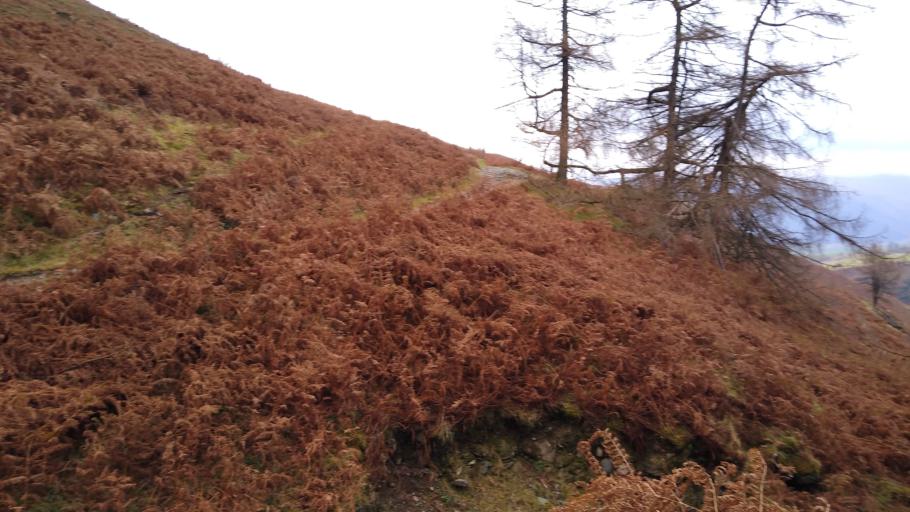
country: GB
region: England
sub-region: Cumbria
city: Keswick
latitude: 54.6236
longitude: -3.1124
